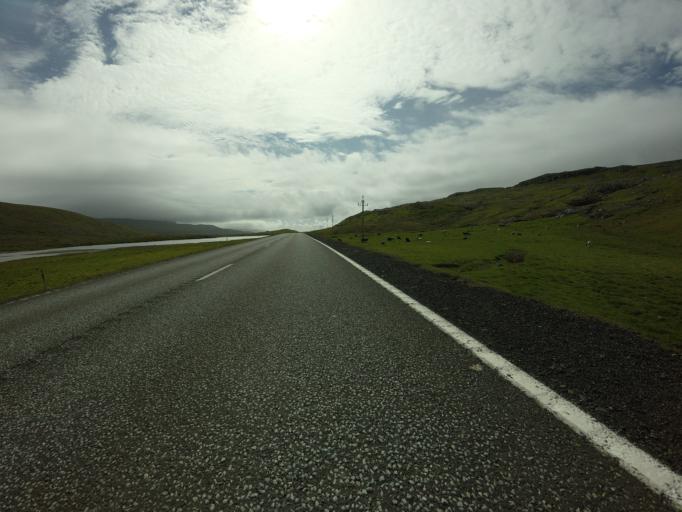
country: FO
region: Sandoy
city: Sandur
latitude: 61.8814
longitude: -6.8658
